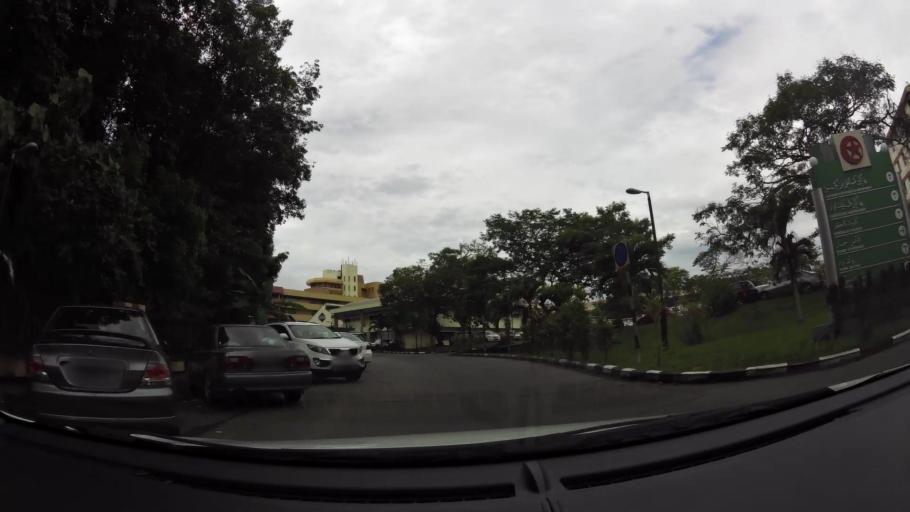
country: BN
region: Brunei and Muara
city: Bandar Seri Begawan
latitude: 4.8933
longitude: 114.9331
